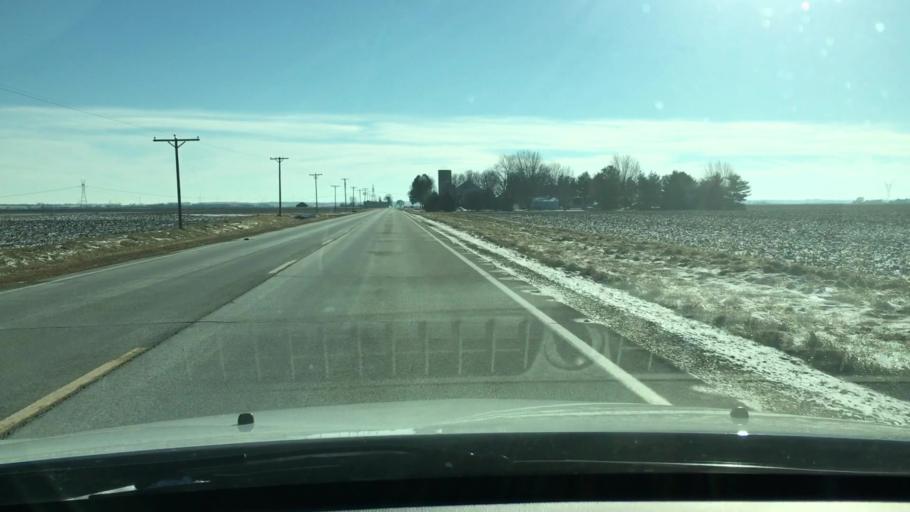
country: US
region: Illinois
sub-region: Ogle County
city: Rochelle
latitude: 41.8094
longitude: -89.0834
